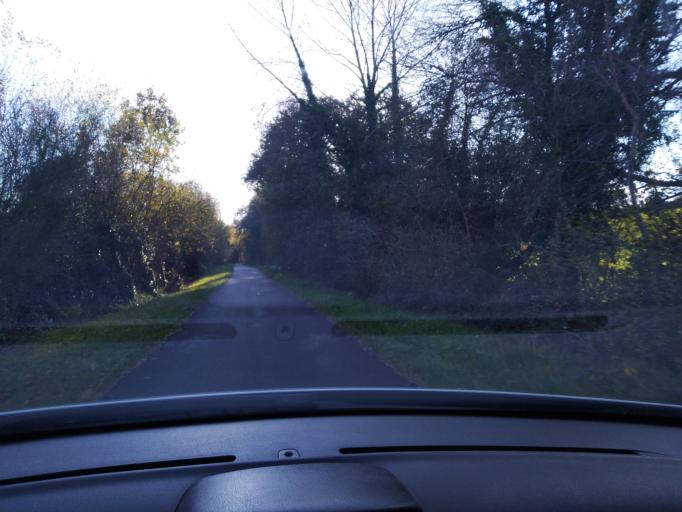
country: FR
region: Brittany
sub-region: Departement du Finistere
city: Guerlesquin
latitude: 48.5121
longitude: -3.5774
